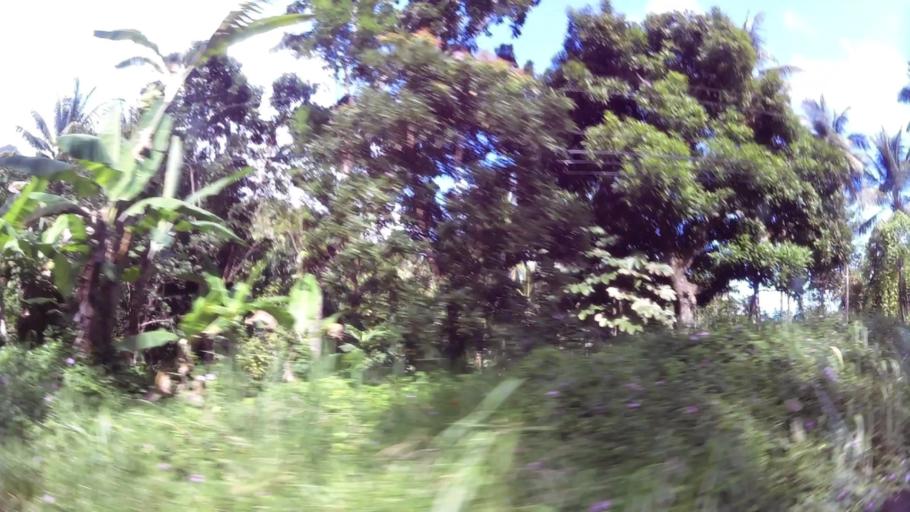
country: DM
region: Saint David
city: Castle Bruce
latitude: 15.4838
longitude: -61.2543
